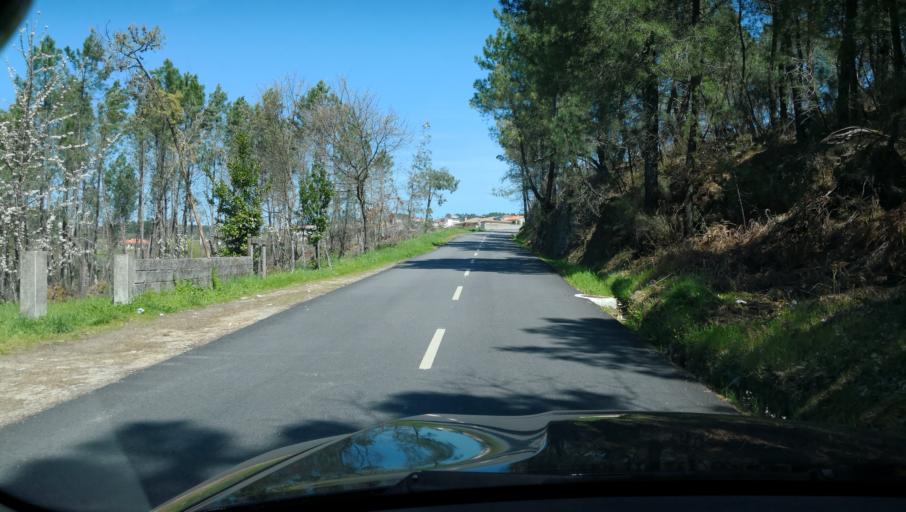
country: PT
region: Vila Real
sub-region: Vila Real
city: Vila Real
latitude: 41.3058
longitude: -7.7031
